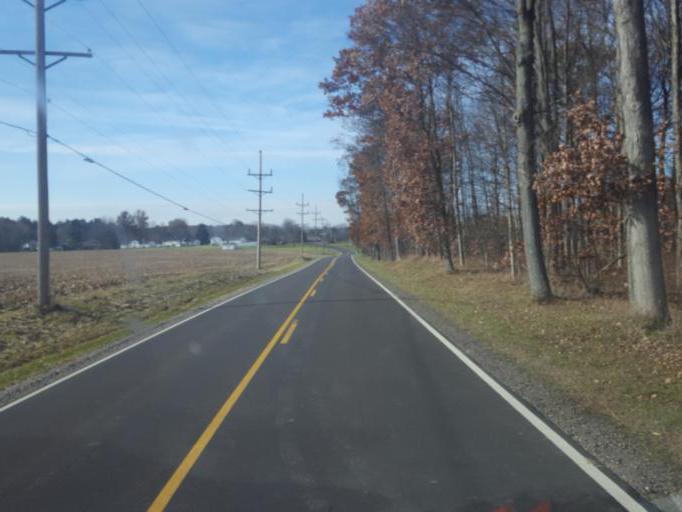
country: US
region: Ohio
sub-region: Crawford County
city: Bucyrus
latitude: 40.8235
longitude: -82.9174
